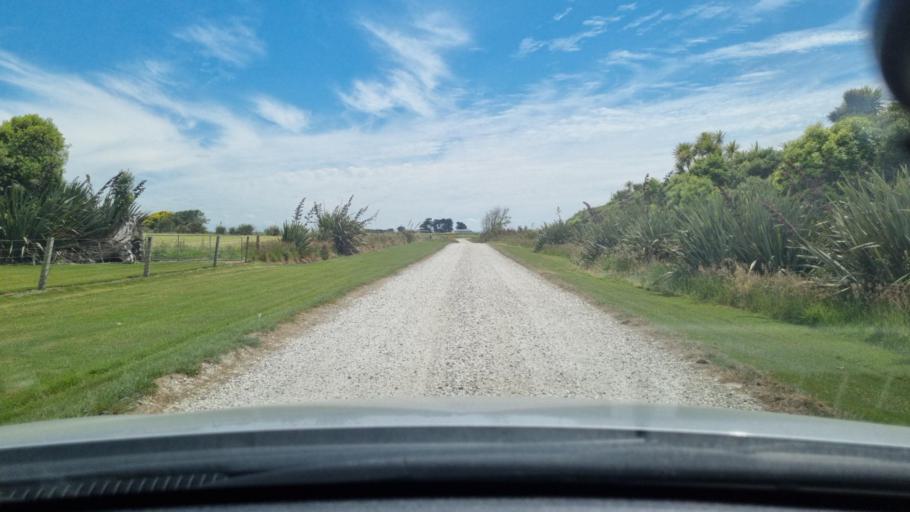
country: NZ
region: Southland
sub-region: Invercargill City
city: Invercargill
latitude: -46.4047
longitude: 168.2603
